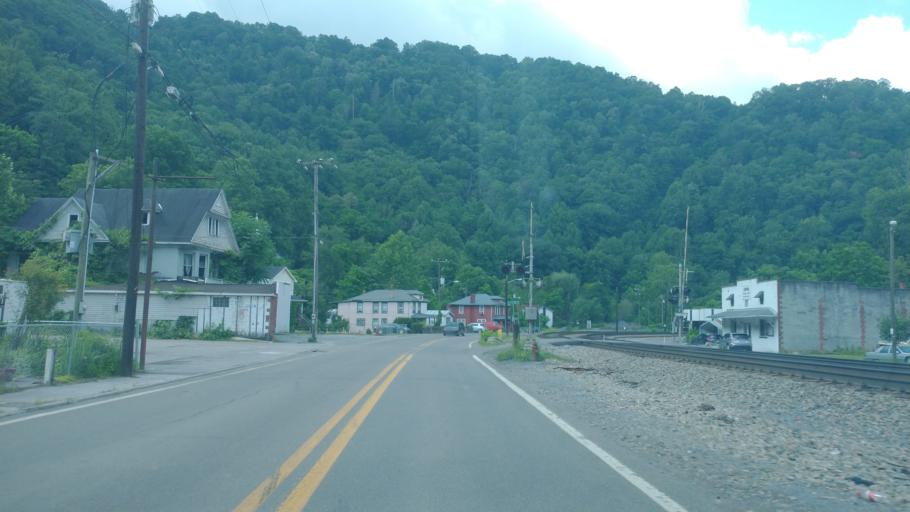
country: US
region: West Virginia
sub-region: McDowell County
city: Welch
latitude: 37.4172
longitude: -81.4441
